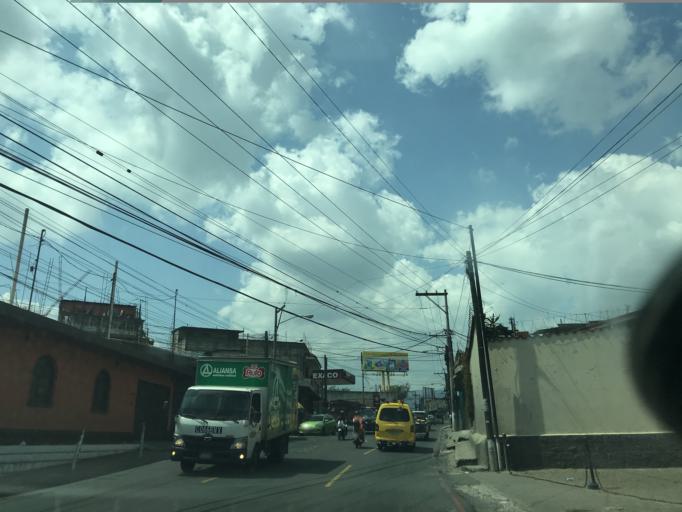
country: GT
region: Guatemala
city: Mixco
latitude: 14.6713
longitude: -90.5740
